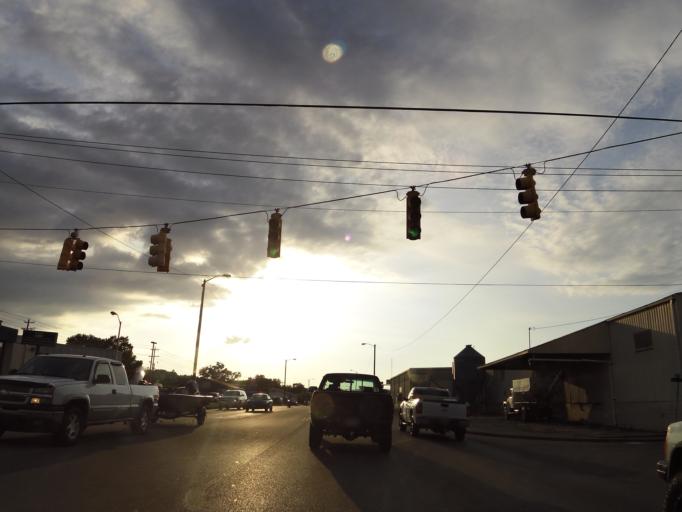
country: US
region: Tennessee
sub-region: Cocke County
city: Newport
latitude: 35.9696
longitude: -83.2055
